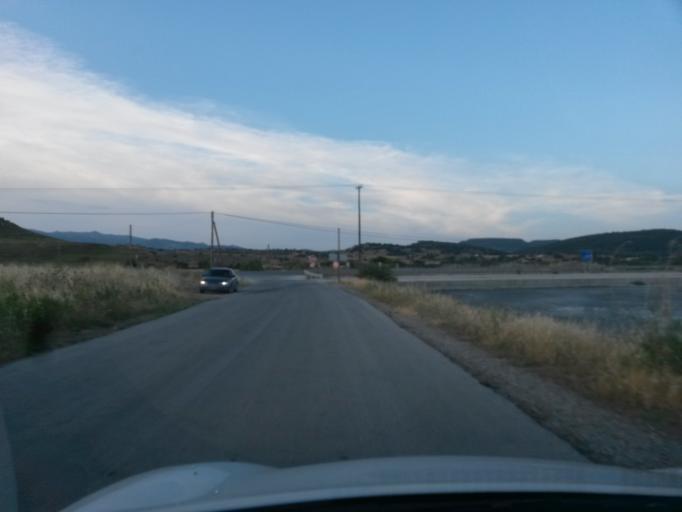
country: GR
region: North Aegean
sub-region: Nomos Lesvou
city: Kalloni
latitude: 39.2252
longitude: 26.2423
